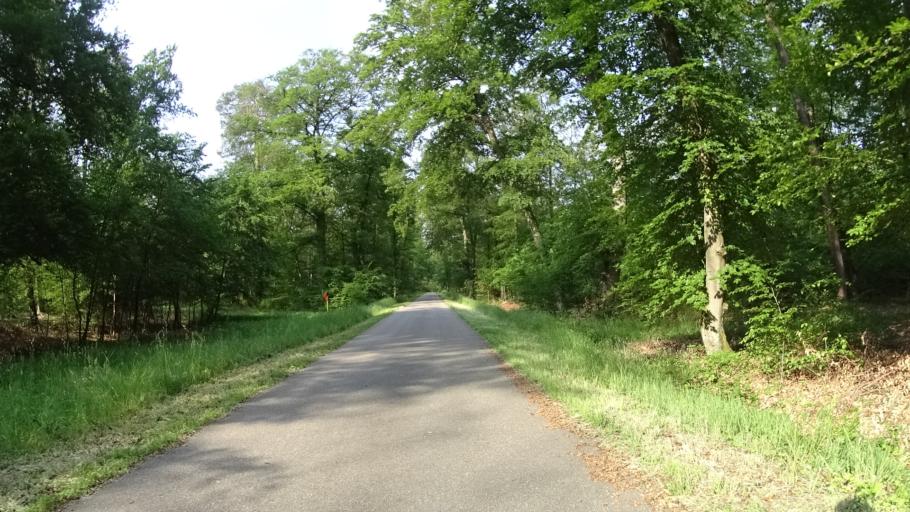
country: DE
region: Baden-Wuerttemberg
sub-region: Karlsruhe Region
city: Walldorf
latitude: 49.3243
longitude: 8.6208
